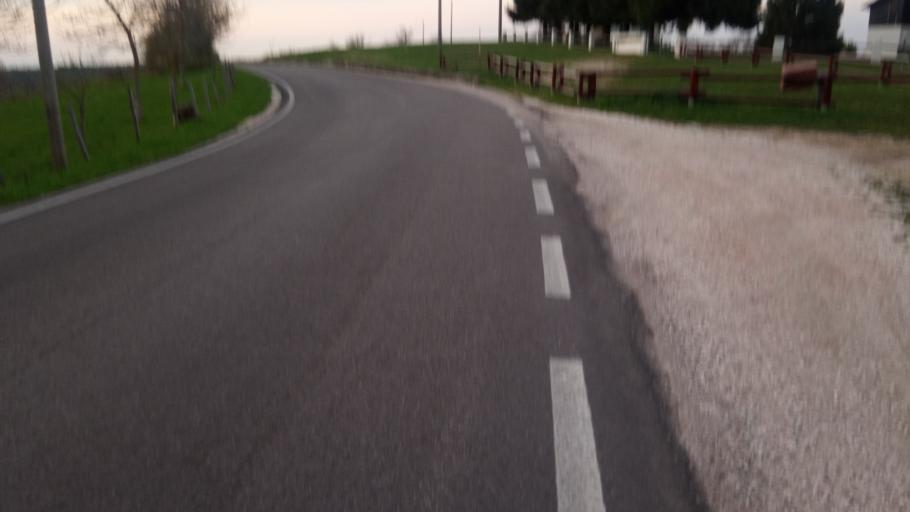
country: IT
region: Veneto
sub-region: Provincia di Vicenza
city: Conco
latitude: 45.8021
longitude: 11.6233
